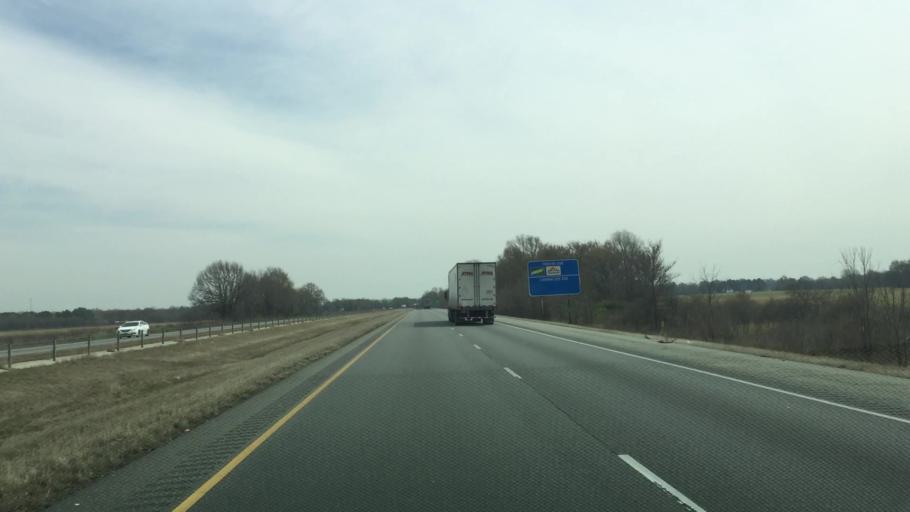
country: US
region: Arkansas
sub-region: Saint Francis County
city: Forrest City
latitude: 34.9757
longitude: -90.9330
